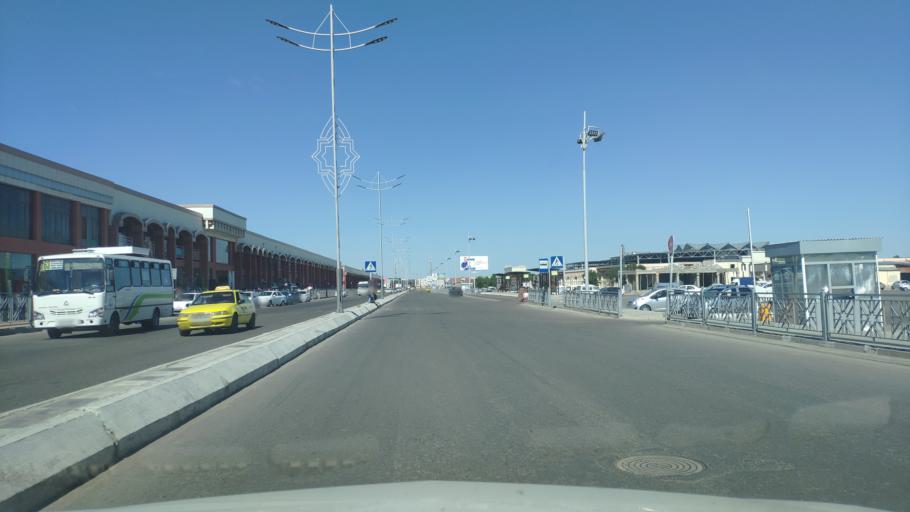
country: UZ
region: Bukhara
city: Bukhara
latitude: 39.7793
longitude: 64.3972
